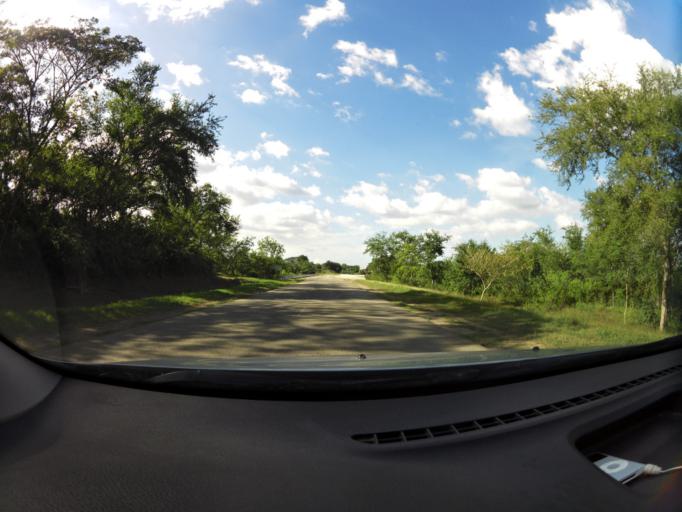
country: CU
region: Santiago de Cuba
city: Palma Soriano
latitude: 20.2519
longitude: -75.9830
